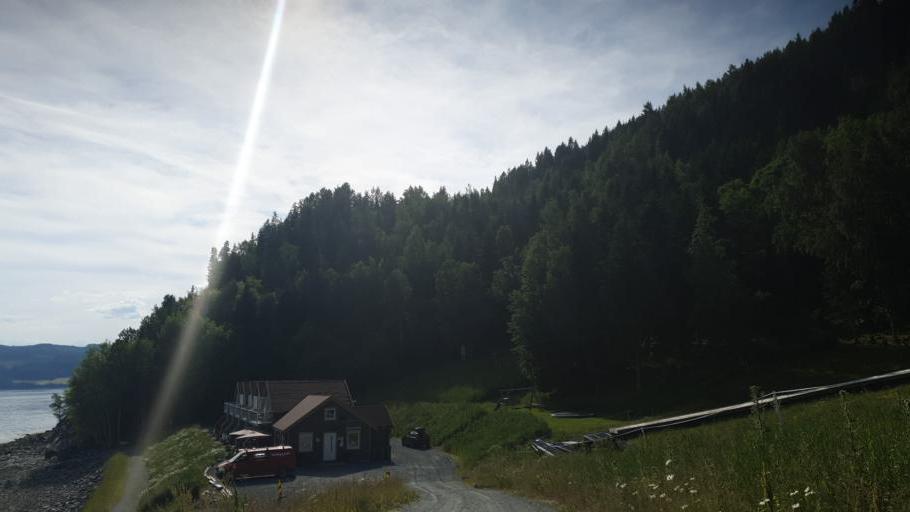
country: NO
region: Nord-Trondelag
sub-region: Leksvik
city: Leksvik
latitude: 63.6796
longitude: 10.6712
